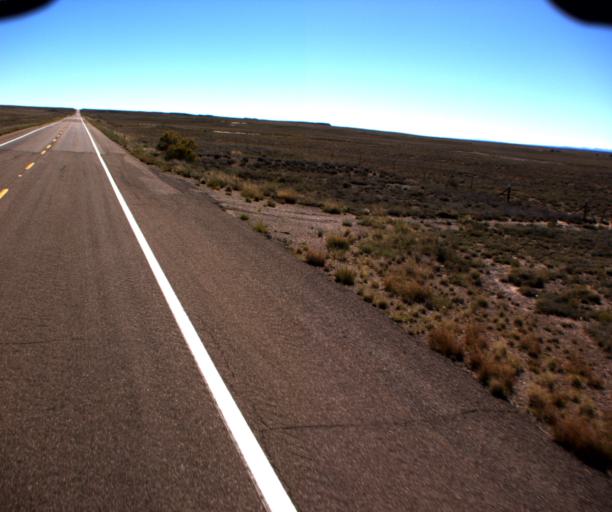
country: US
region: Arizona
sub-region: Navajo County
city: Holbrook
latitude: 34.7855
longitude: -109.8693
